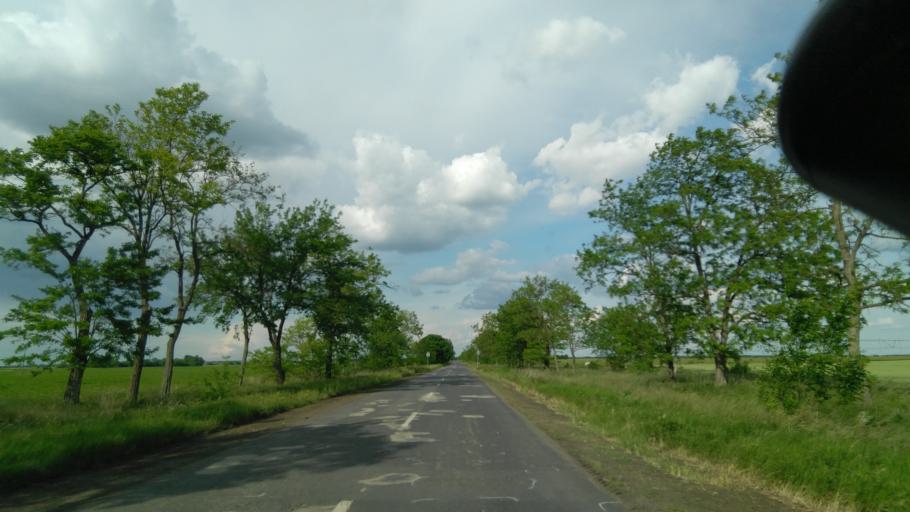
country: HU
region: Bekes
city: Battonya
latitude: 46.3026
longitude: 21.0547
